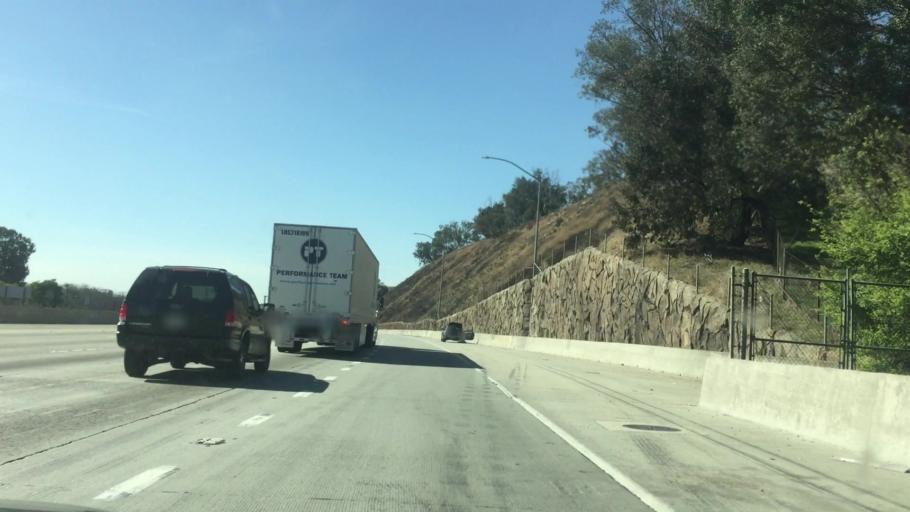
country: US
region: California
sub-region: Los Angeles County
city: La Verne
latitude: 34.0722
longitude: -117.7914
